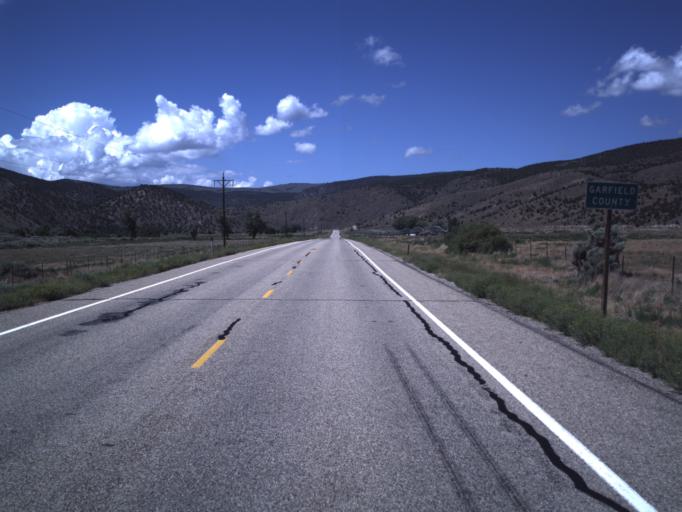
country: US
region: Utah
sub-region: Piute County
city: Junction
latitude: 38.1499
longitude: -112.2931
